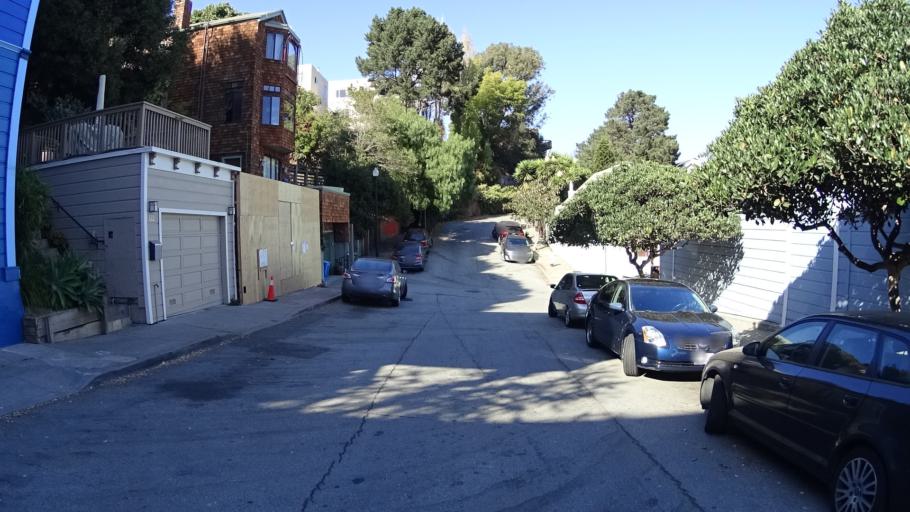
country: US
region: California
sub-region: San Francisco County
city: San Francisco
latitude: 37.7447
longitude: -122.4070
